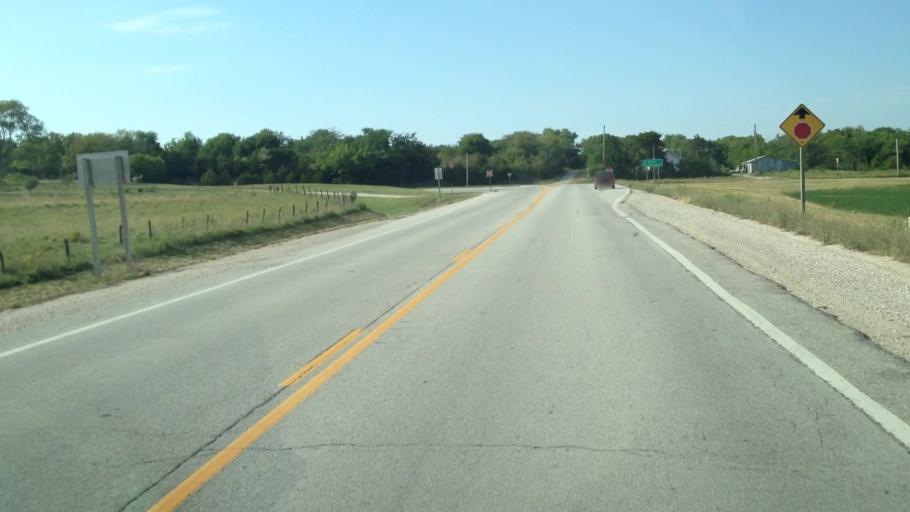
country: US
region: Kansas
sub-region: Anderson County
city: Garnett
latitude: 38.0796
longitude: -95.1694
